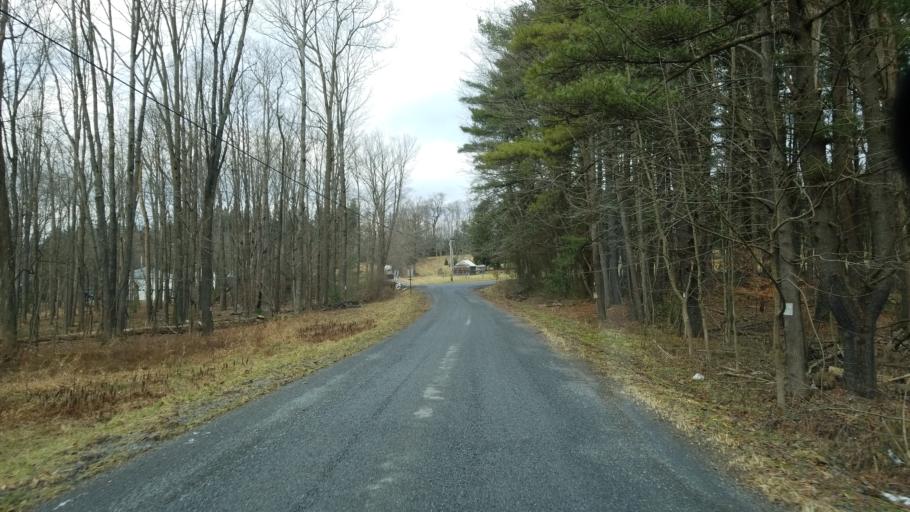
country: US
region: Pennsylvania
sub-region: Clearfield County
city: Clearfield
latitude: 41.1450
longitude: -78.5467
